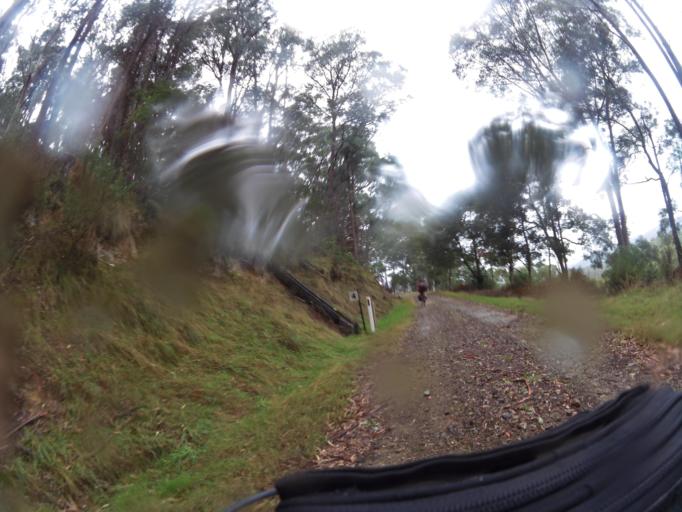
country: AU
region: New South Wales
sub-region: Greater Hume Shire
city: Holbrook
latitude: -36.2199
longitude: 147.5634
